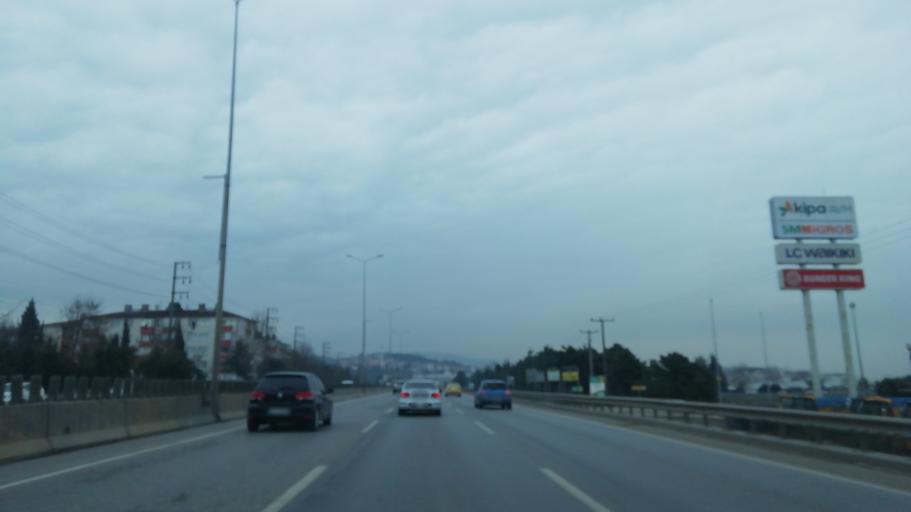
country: TR
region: Kocaeli
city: Derince
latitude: 40.7598
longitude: 29.8469
